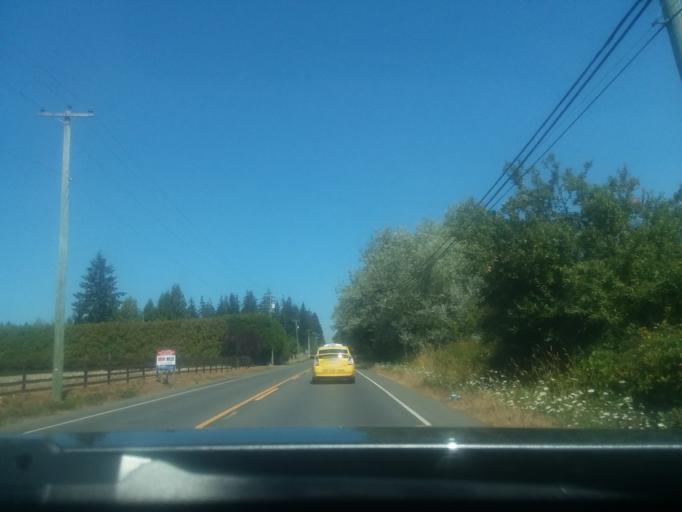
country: CA
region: British Columbia
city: Courtenay
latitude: 49.6983
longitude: -124.9344
